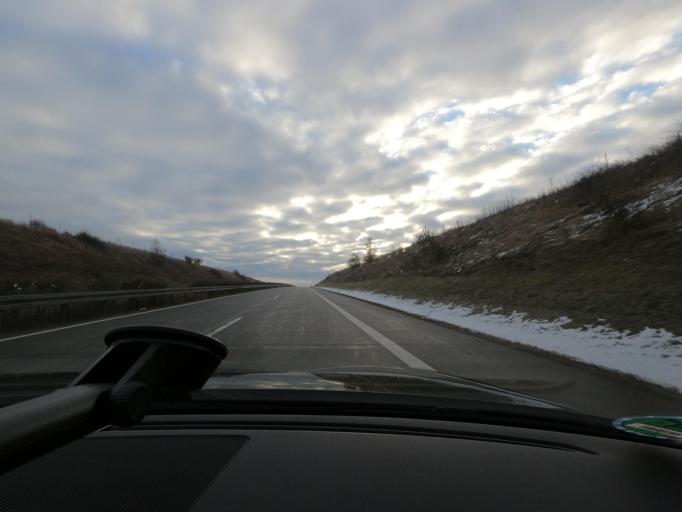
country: DE
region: Thuringia
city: Eisfeld
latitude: 50.4517
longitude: 10.8650
